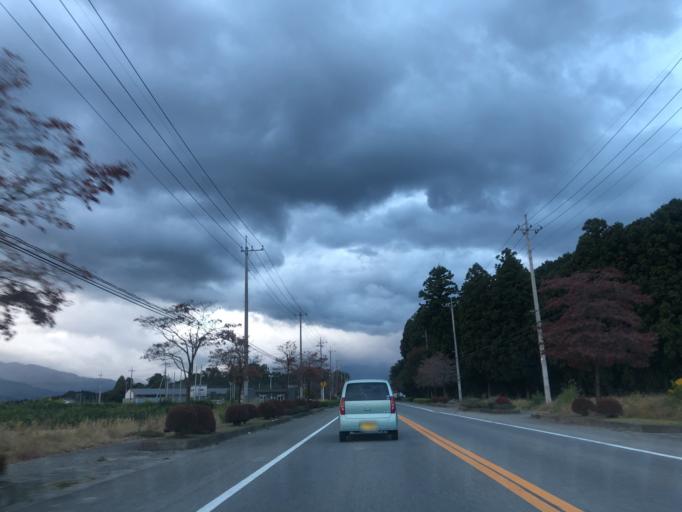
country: JP
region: Tochigi
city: Kuroiso
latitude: 36.9445
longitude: 140.0069
